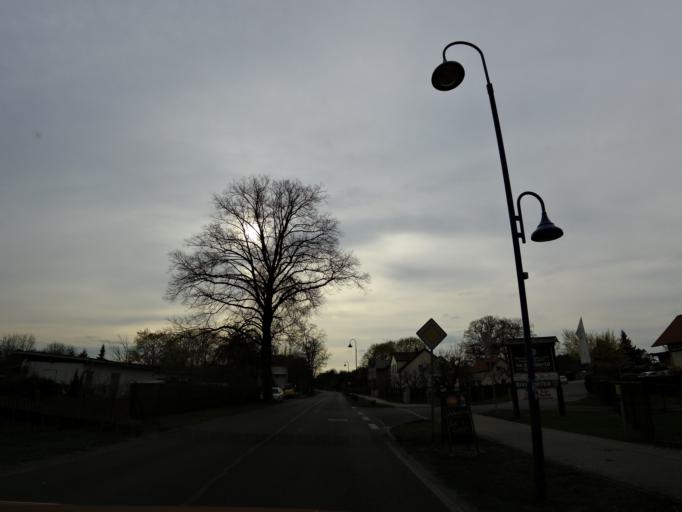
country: DE
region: Brandenburg
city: Bestensee
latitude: 52.2432
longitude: 13.6245
